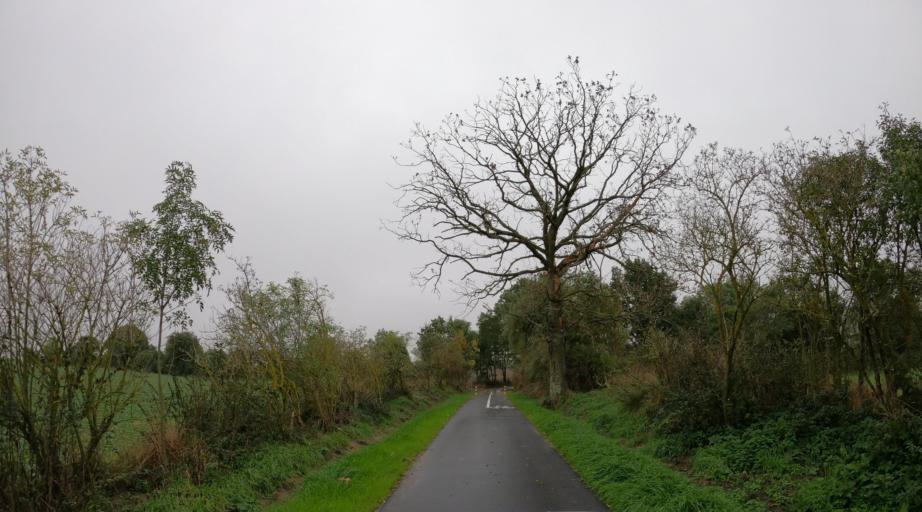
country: PL
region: West Pomeranian Voivodeship
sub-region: Powiat mysliborski
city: Mysliborz
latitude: 52.9163
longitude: 14.7436
